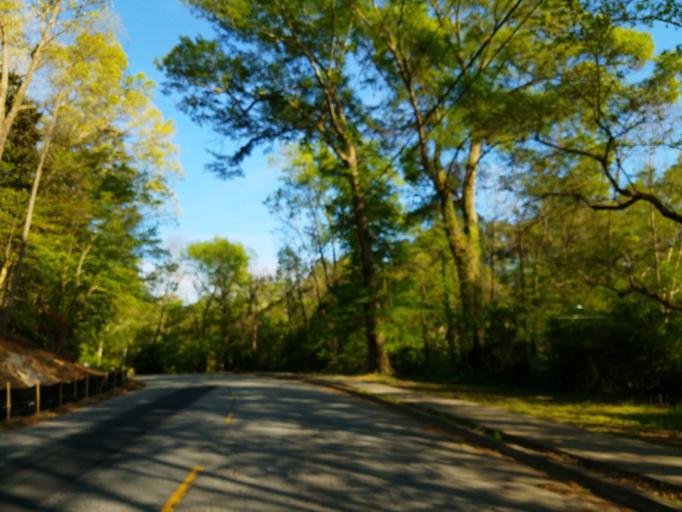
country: US
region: Georgia
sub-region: Cobb County
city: Vinings
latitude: 33.8249
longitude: -84.4144
